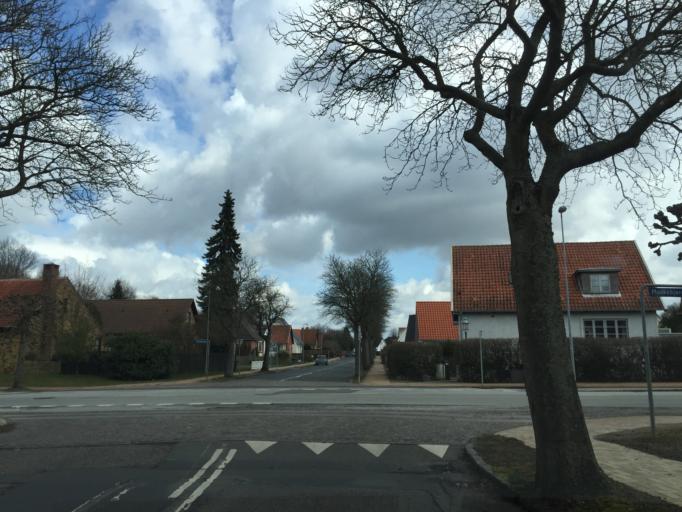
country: DK
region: South Denmark
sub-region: Odense Kommune
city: Odense
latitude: 55.3846
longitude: 10.4047
